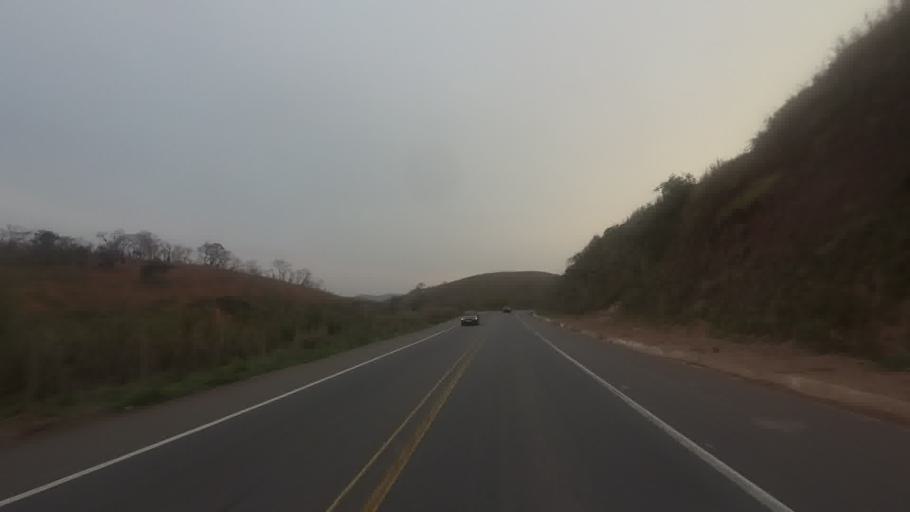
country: BR
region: Rio de Janeiro
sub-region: Carmo
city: Carmo
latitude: -21.7553
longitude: -42.4798
